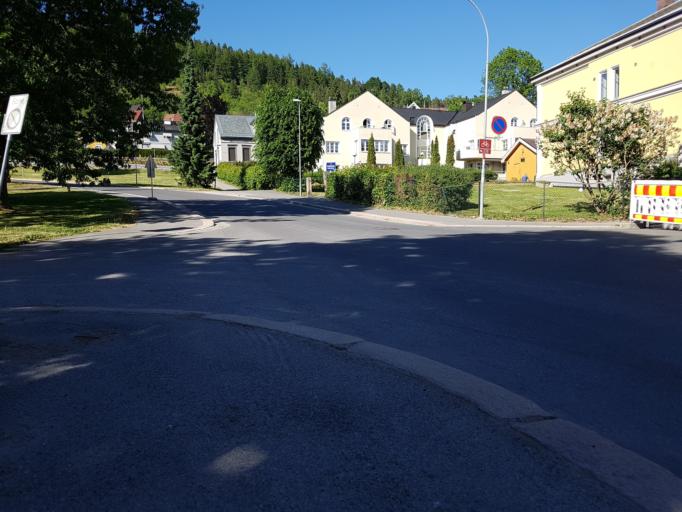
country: NO
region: Buskerud
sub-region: Drammen
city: Drammen
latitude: 59.7462
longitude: 10.2076
